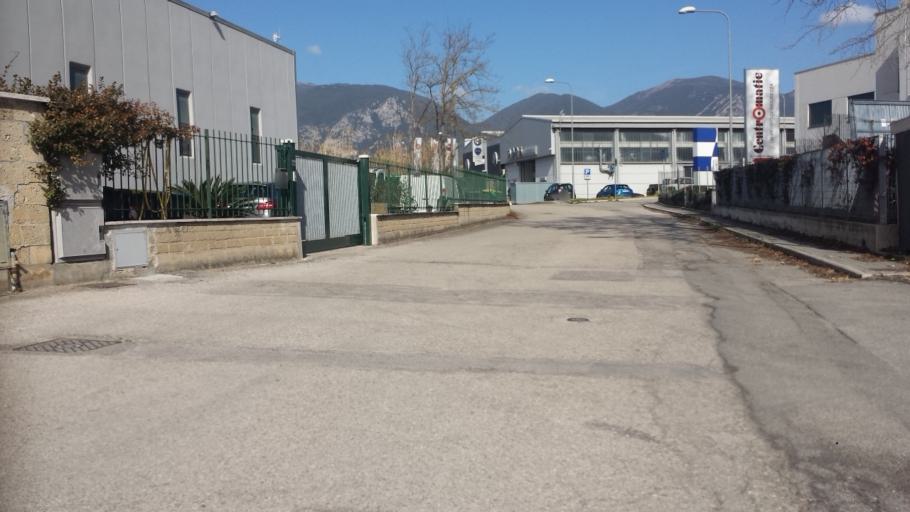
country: IT
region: Umbria
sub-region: Provincia di Terni
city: Terni
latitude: 42.5658
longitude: 12.5994
